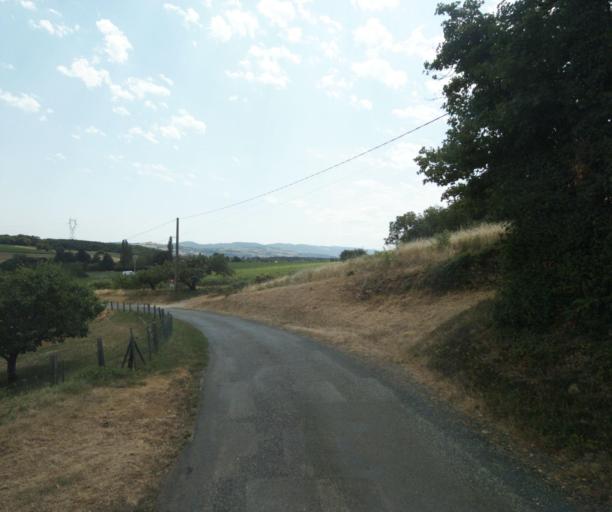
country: FR
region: Rhone-Alpes
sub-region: Departement du Rhone
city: Chatillon
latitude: 45.8762
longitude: 4.6214
